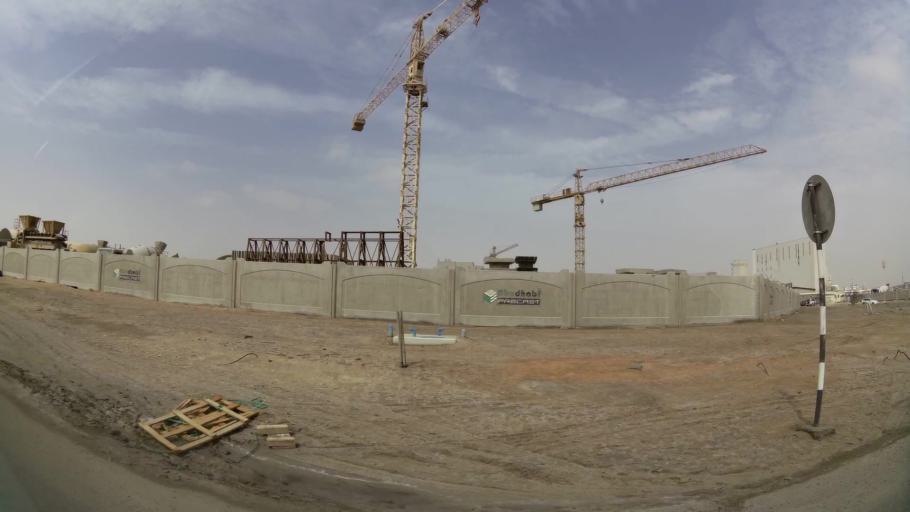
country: AE
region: Abu Dhabi
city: Abu Dhabi
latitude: 24.3290
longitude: 54.4920
